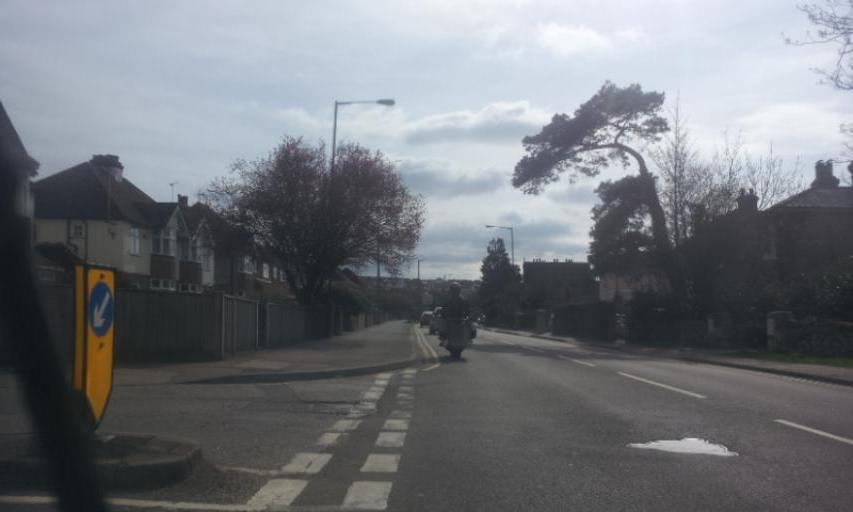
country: GB
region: England
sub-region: Kent
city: Whitstable
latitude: 51.3521
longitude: 1.0233
